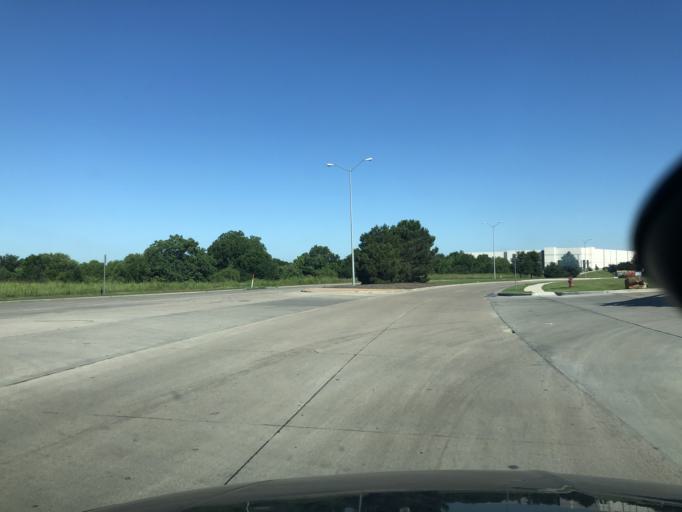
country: US
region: Texas
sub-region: Tarrant County
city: Euless
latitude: 32.8014
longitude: -97.0309
